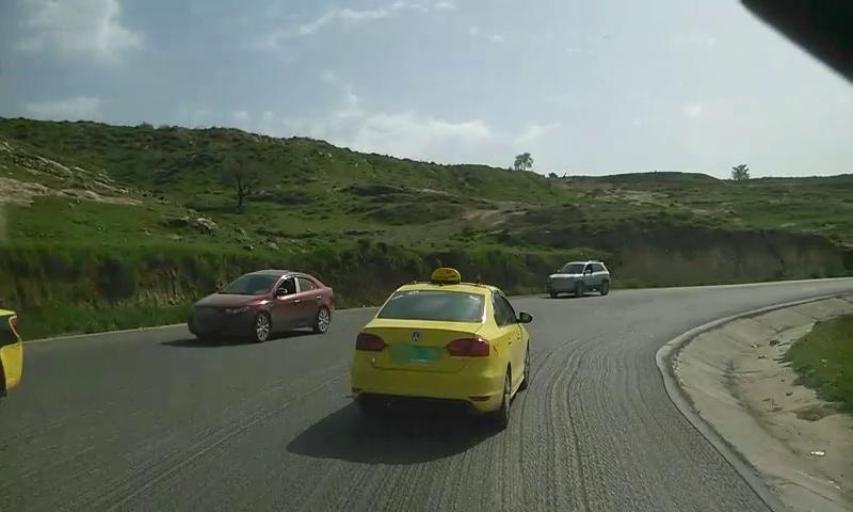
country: PS
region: West Bank
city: Mirkah
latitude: 32.3832
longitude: 35.2177
